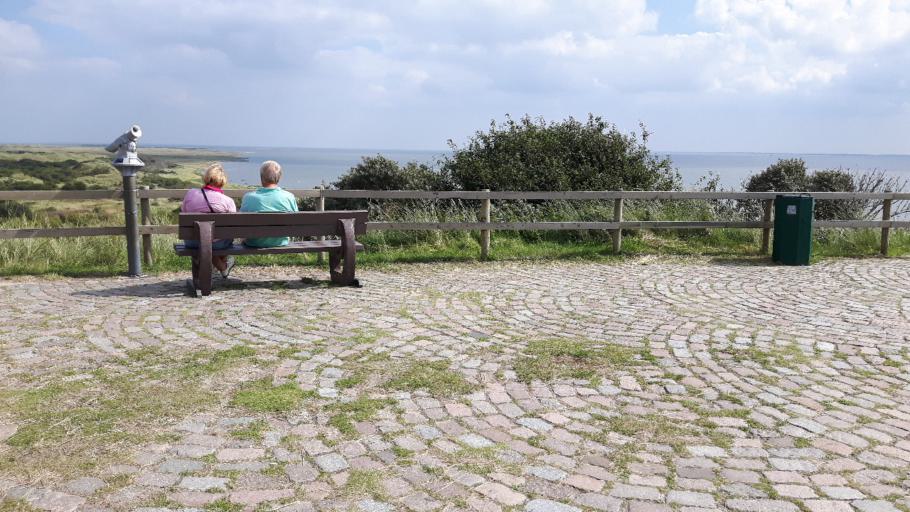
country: NL
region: Friesland
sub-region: Gemeente Dongeradeel
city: Holwerd
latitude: 53.4575
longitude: 5.9031
